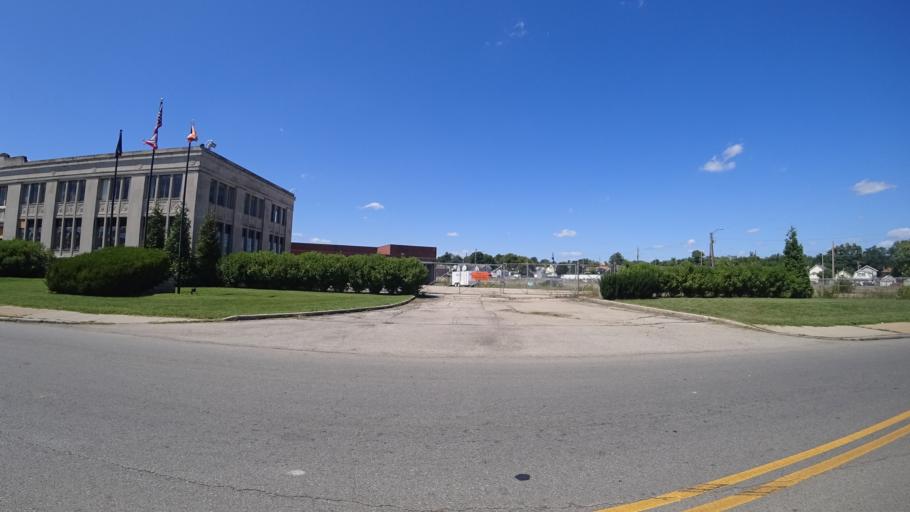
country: US
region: Ohio
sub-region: Butler County
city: Hamilton
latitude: 39.4106
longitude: -84.5599
